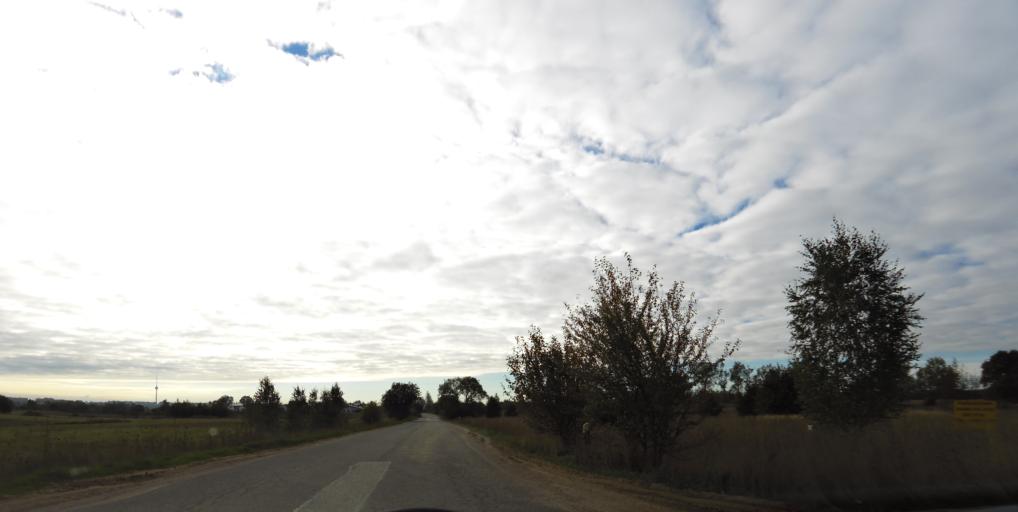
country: LT
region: Vilnius County
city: Pilaite
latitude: 54.7246
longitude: 25.1526
